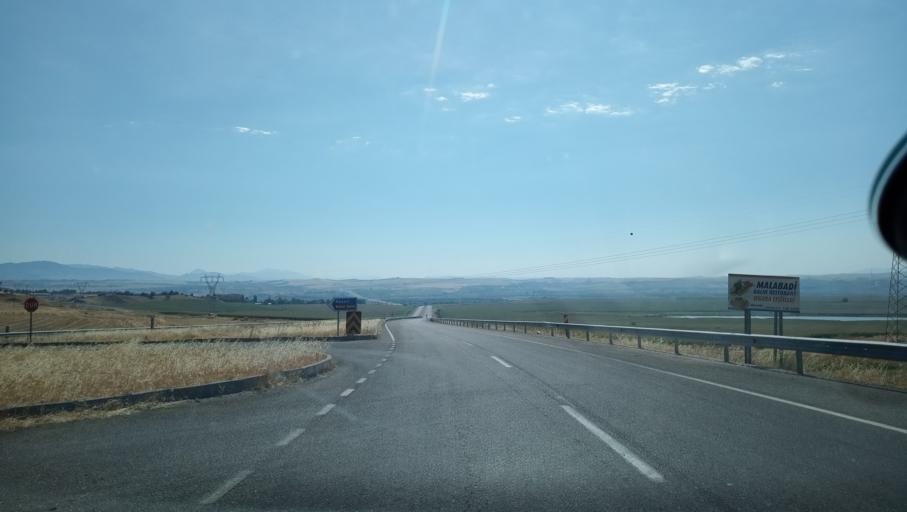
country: TR
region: Diyarbakir
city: Malabadi
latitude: 38.1281
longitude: 41.1754
